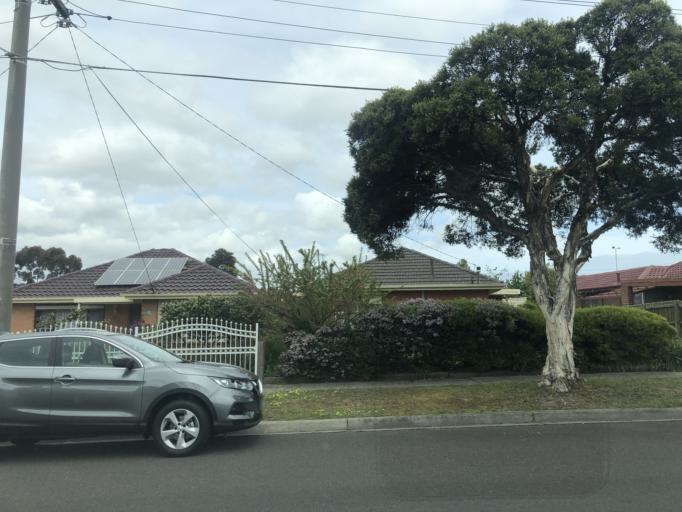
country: AU
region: Victoria
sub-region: Greater Dandenong
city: Dandenong North
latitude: -37.9553
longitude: 145.2053
